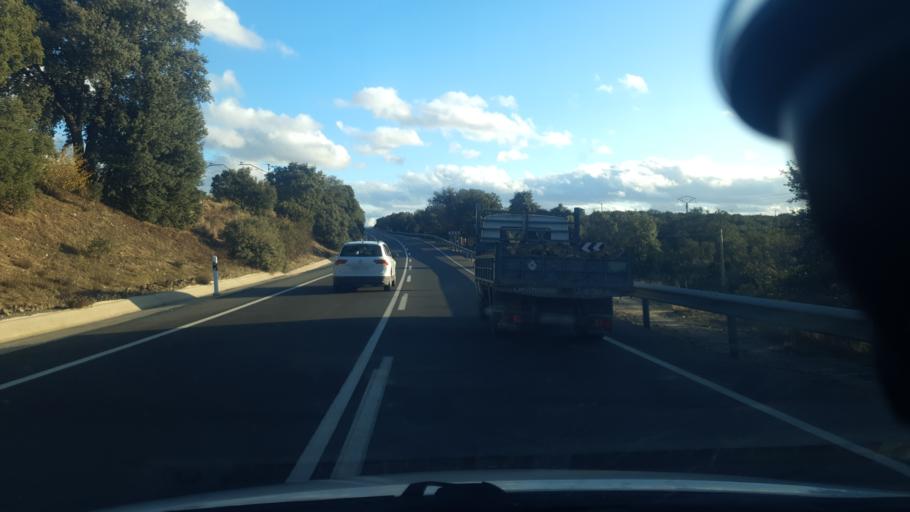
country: ES
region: Castille and Leon
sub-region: Provincia de Avila
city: Mingorria
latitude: 40.7153
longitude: -4.6741
